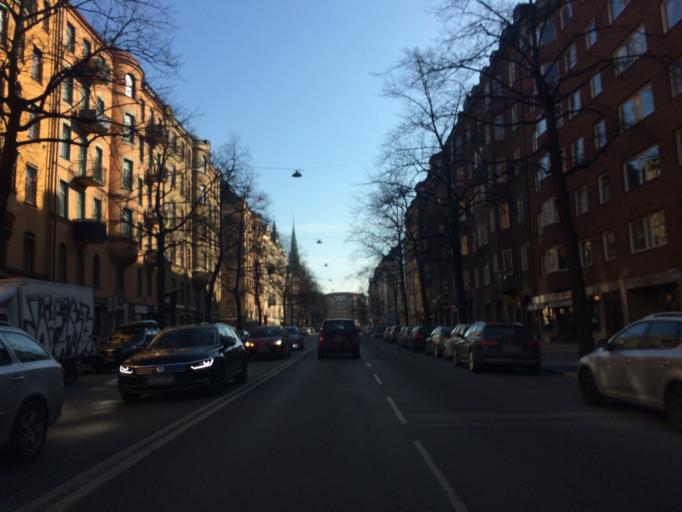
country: SE
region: Stockholm
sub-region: Stockholms Kommun
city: Stockholm
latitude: 59.3480
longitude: 18.0602
